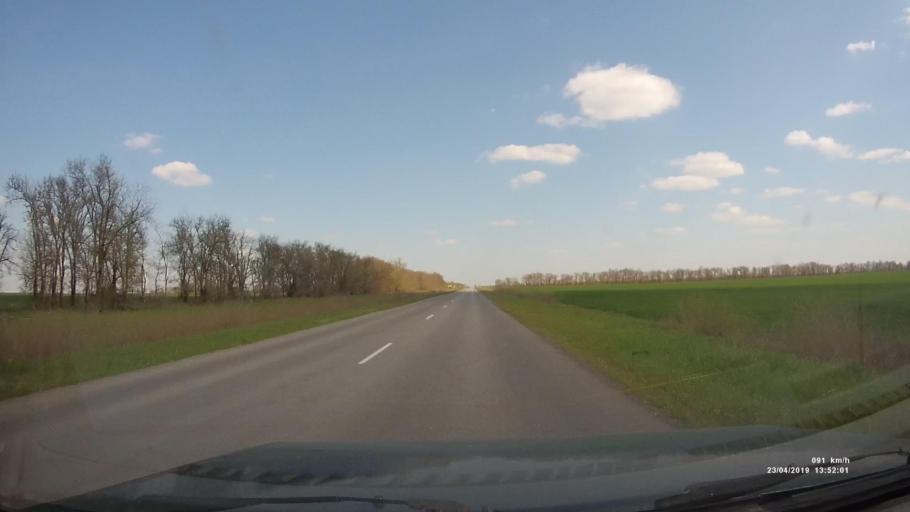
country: RU
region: Rostov
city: Remontnoye
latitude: 46.5999
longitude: 42.9464
